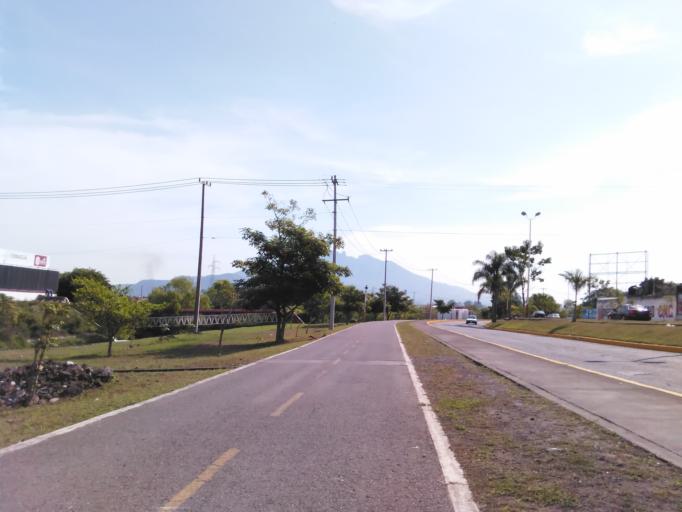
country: MX
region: Nayarit
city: Tepic
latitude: 21.4878
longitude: -104.8535
